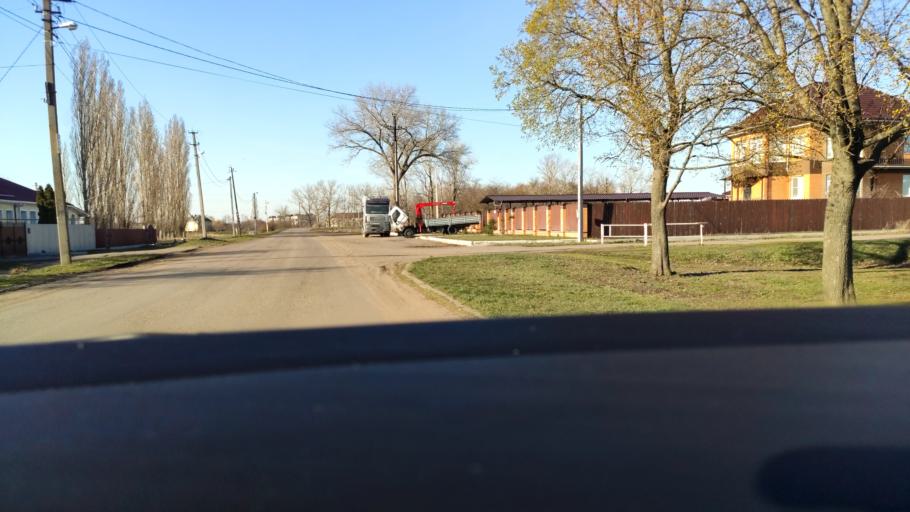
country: RU
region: Voronezj
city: Maslovka
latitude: 51.5076
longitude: 39.2939
